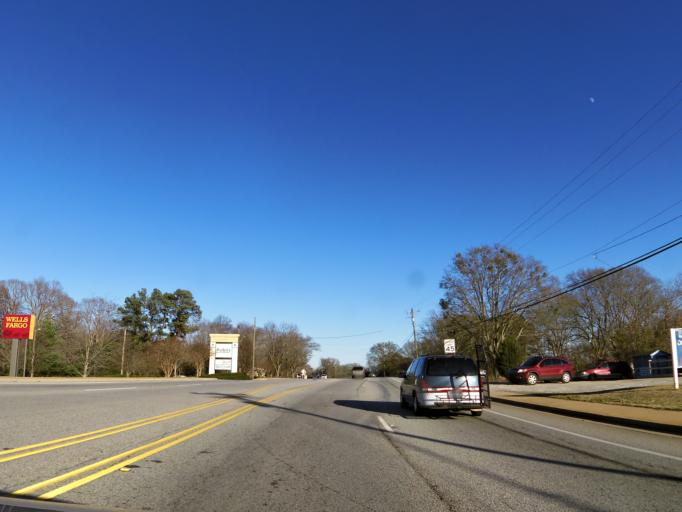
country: US
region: South Carolina
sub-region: Spartanburg County
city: Wellford
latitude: 34.8869
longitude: -82.0663
